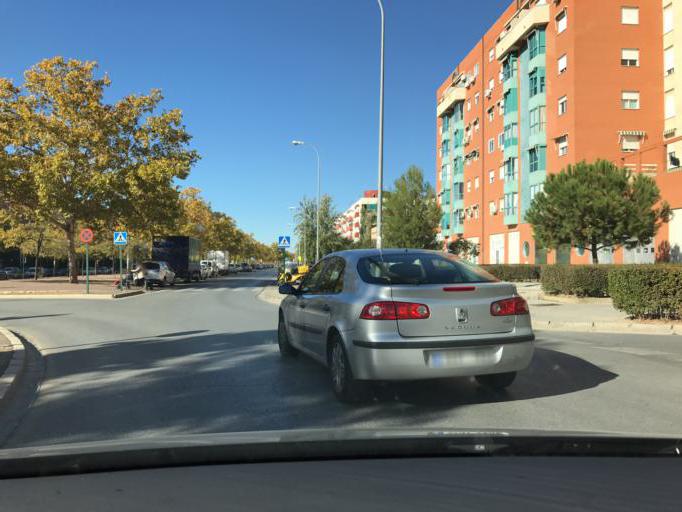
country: ES
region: Andalusia
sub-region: Provincia de Granada
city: Granada
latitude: 37.2034
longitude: -3.6103
